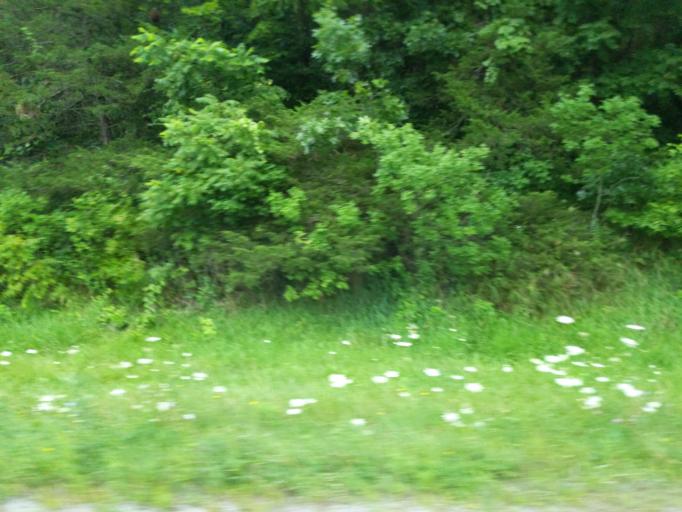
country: US
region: Wisconsin
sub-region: Sauk County
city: Sauk City
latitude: 43.2409
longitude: -89.7273
